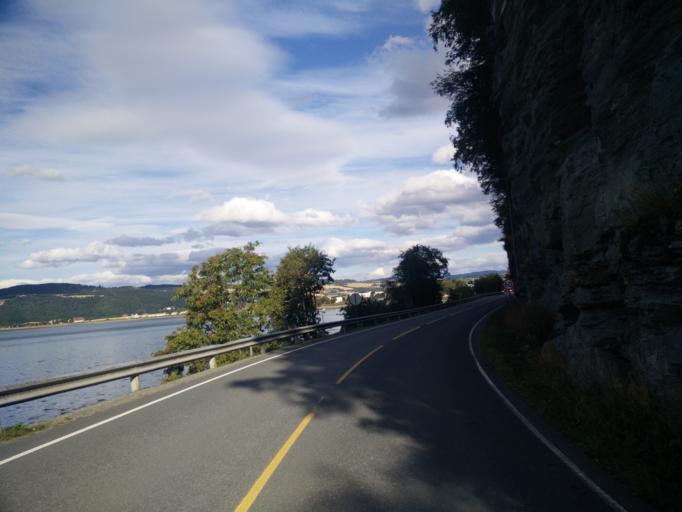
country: NO
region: Sor-Trondelag
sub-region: Melhus
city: Melhus
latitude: 63.3225
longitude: 10.2039
